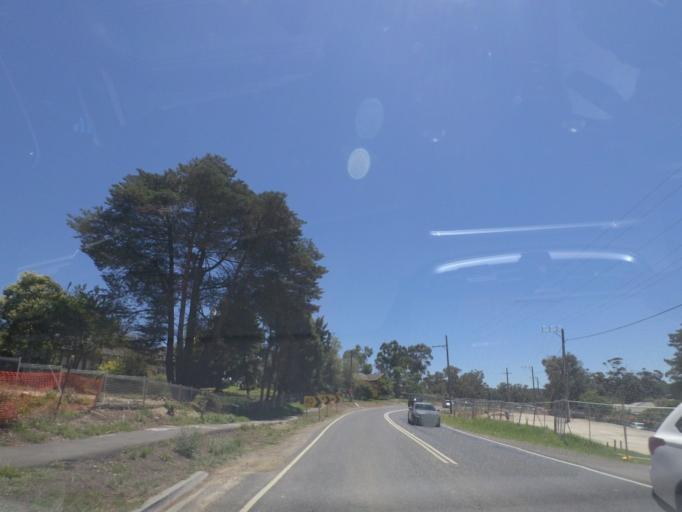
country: AU
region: Victoria
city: Plenty
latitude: -37.6642
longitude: 145.1237
